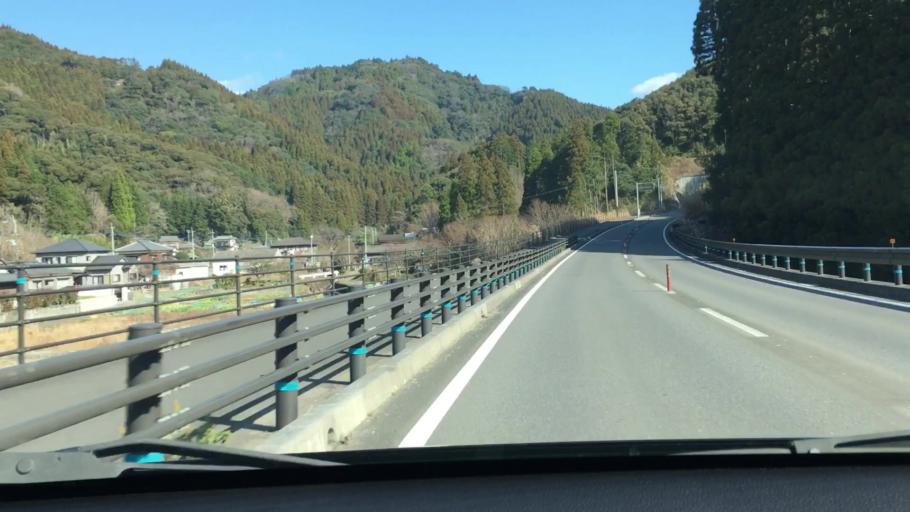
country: JP
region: Oita
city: Saiki
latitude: 32.9593
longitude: 131.8470
